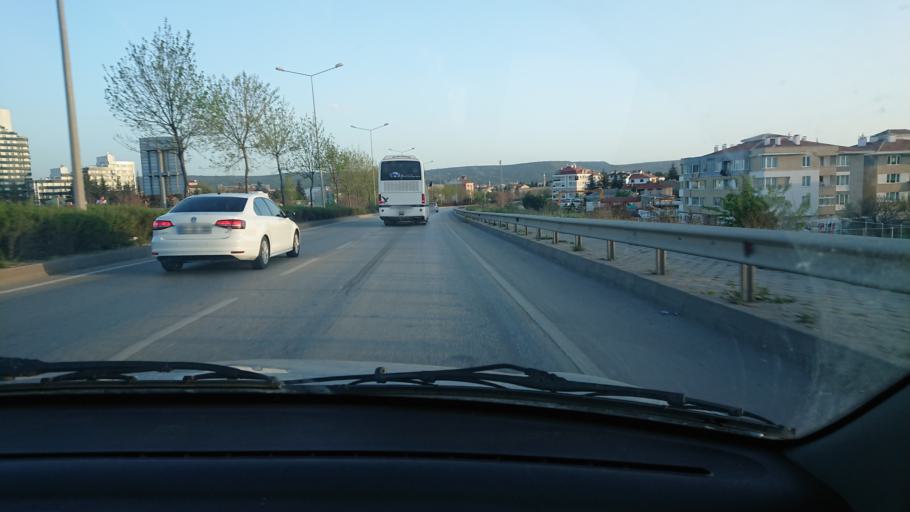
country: TR
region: Eskisehir
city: Eskisehir
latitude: 39.7743
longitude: 30.4837
